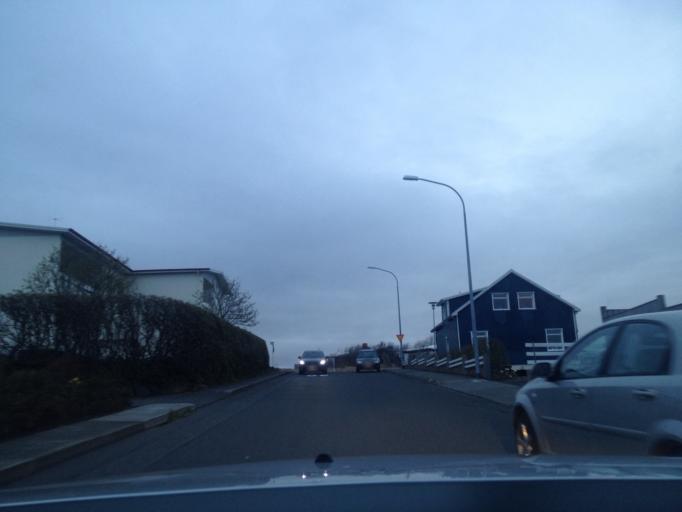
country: IS
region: Capital Region
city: Seltjarnarnes
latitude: 64.1543
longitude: -21.9996
